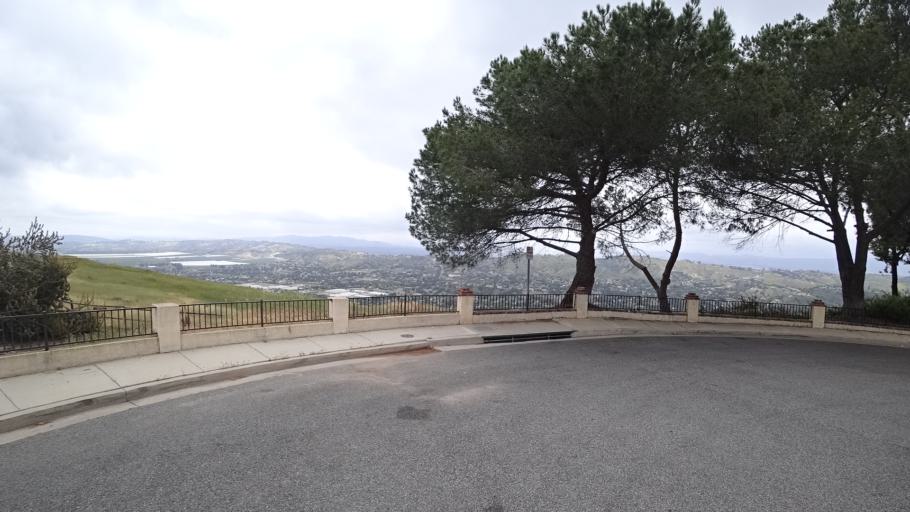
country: US
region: California
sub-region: Ventura County
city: Casa Conejo
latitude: 34.2276
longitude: -118.9021
